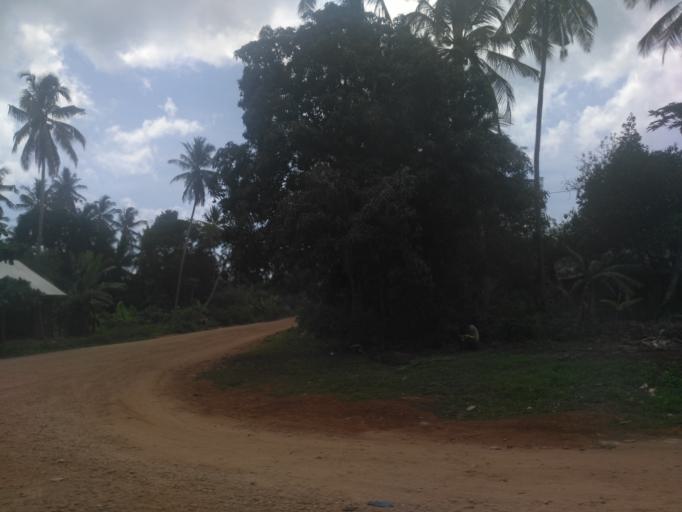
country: TZ
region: Zanzibar Urban/West
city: Zanzibar
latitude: -6.2609
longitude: 39.2611
